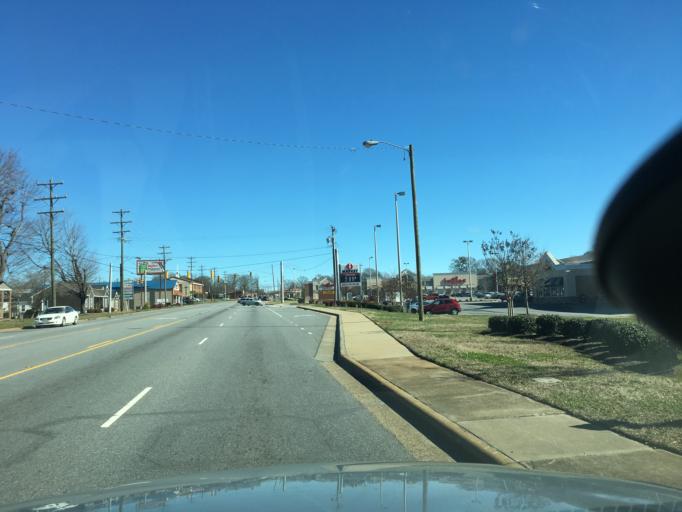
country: US
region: North Carolina
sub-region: Lincoln County
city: Lincolnton
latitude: 35.4787
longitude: -81.2229
